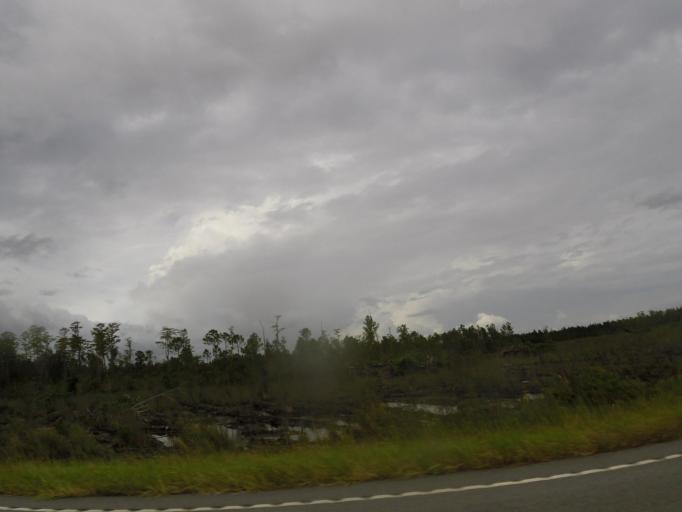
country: US
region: Florida
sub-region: Nassau County
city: Hilliard
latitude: 30.5215
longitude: -82.0599
